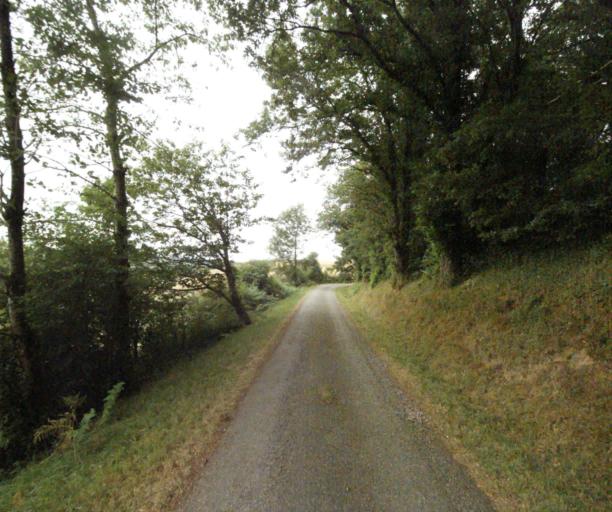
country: FR
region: Midi-Pyrenees
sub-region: Departement du Tarn
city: Soreze
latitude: 43.3911
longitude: 2.0552
